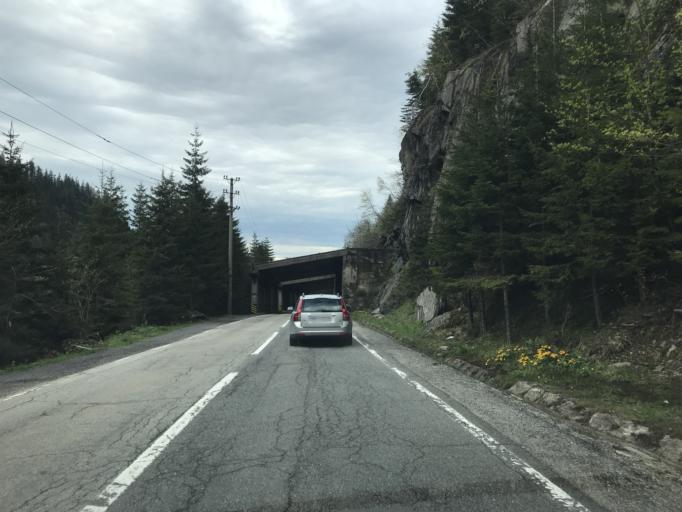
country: RO
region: Sibiu
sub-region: Comuna Cartisoara
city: Cartisoara
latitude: 45.6385
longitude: 24.6057
